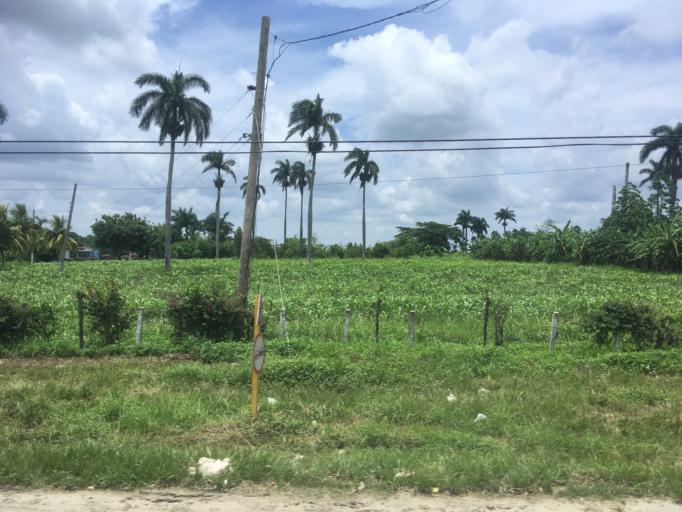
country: CU
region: Villa Clara
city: Esperanza
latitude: 22.4126
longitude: -80.0384
